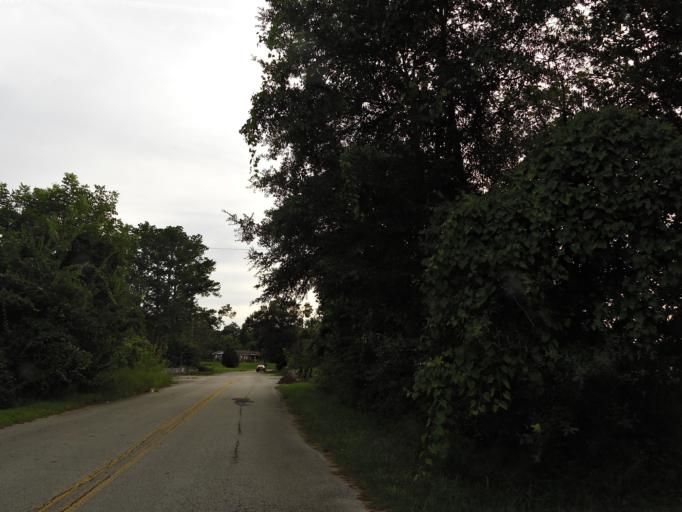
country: US
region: Florida
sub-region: Duval County
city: Jacksonville
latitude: 30.3982
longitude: -81.6988
